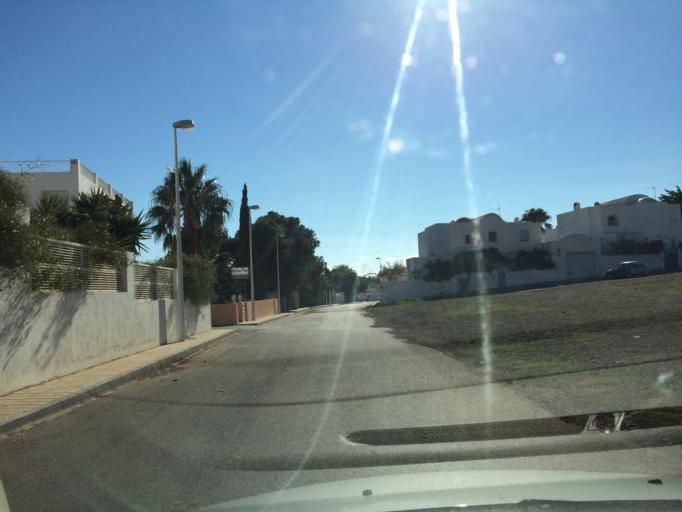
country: ES
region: Andalusia
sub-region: Provincia de Almeria
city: San Jose
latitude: 36.7668
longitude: -2.1106
